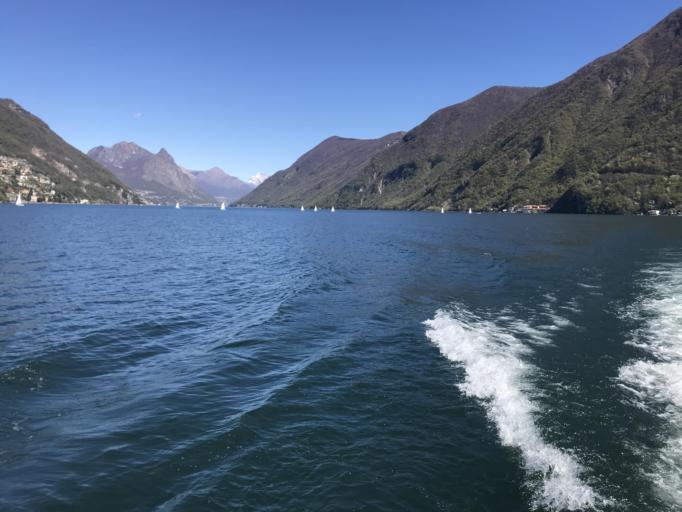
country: CH
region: Ticino
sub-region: Lugano District
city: Lugano
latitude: 45.9894
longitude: 8.9624
